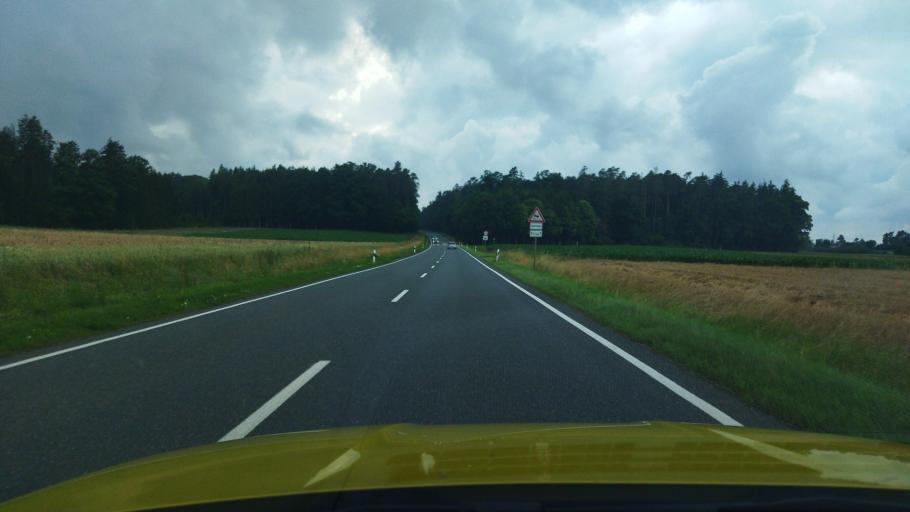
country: DE
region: Bavaria
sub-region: Regierungsbezirk Mittelfranken
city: Absberg
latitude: 49.1137
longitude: 10.8749
